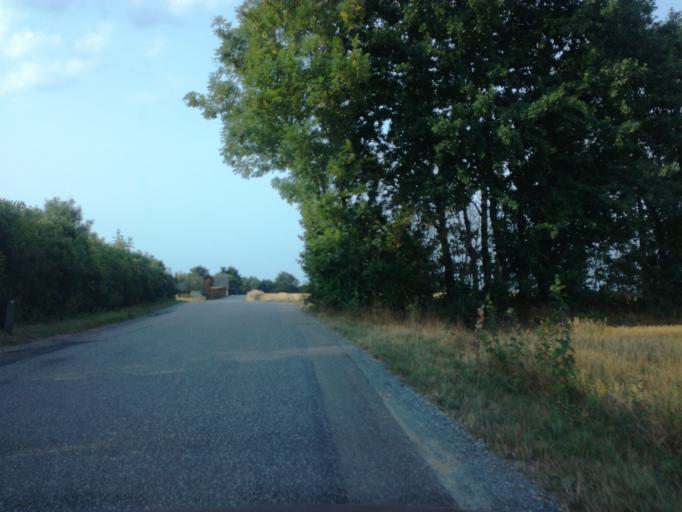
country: DK
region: South Denmark
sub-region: Vejle Kommune
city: Vejle
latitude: 55.6559
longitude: 9.5457
